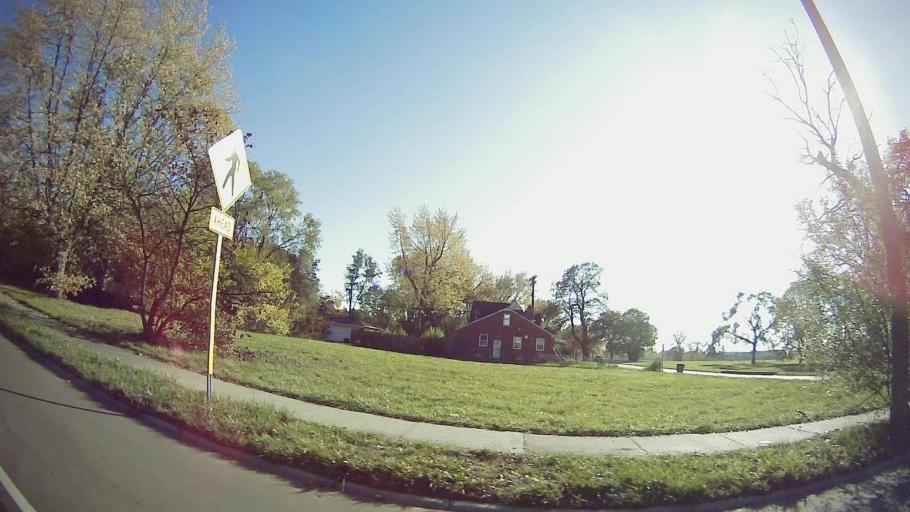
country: US
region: Michigan
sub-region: Macomb County
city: Warren
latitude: 42.4345
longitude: -82.9999
